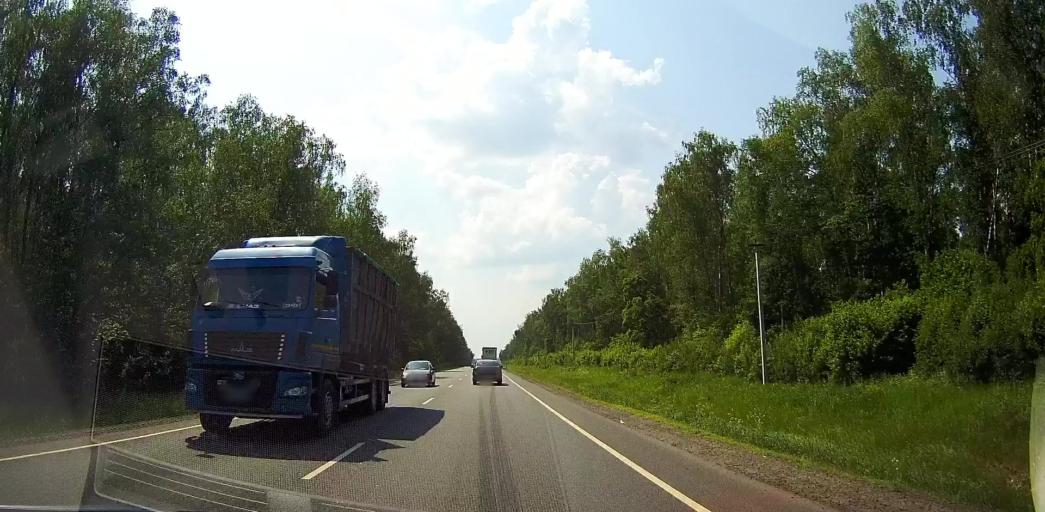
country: RU
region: Moskovskaya
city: Meshcherino
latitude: 55.1400
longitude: 38.2756
